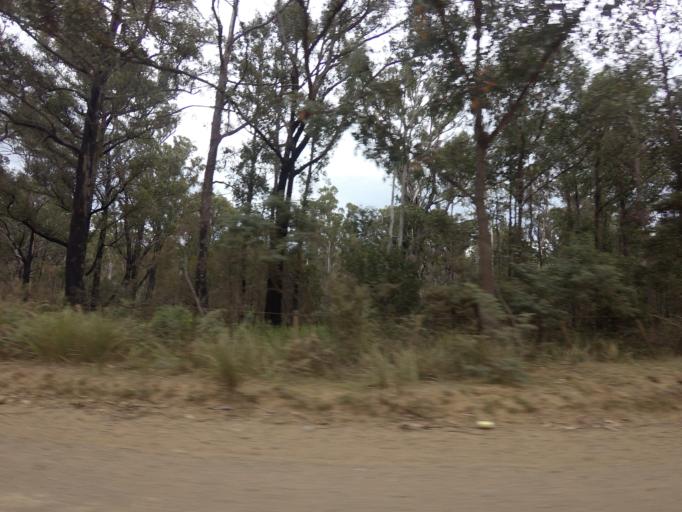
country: AU
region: Tasmania
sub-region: Derwent Valley
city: New Norfolk
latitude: -42.5636
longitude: 146.9672
